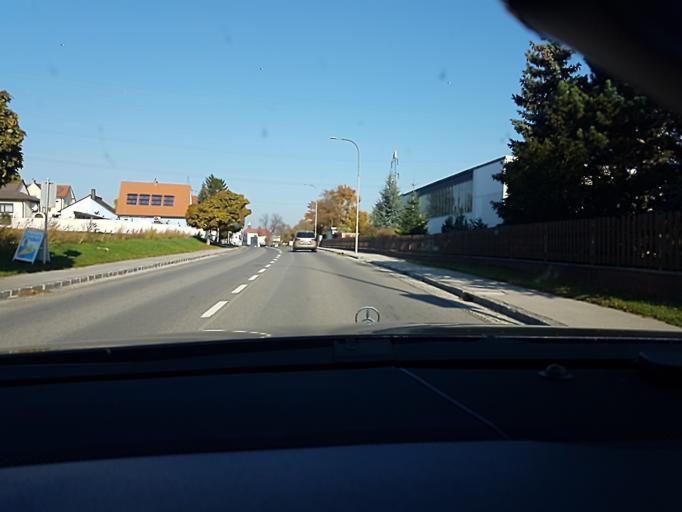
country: AT
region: Lower Austria
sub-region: Politischer Bezirk Wien-Umgebung
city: Lanzendorf
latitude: 48.1022
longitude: 16.4299
